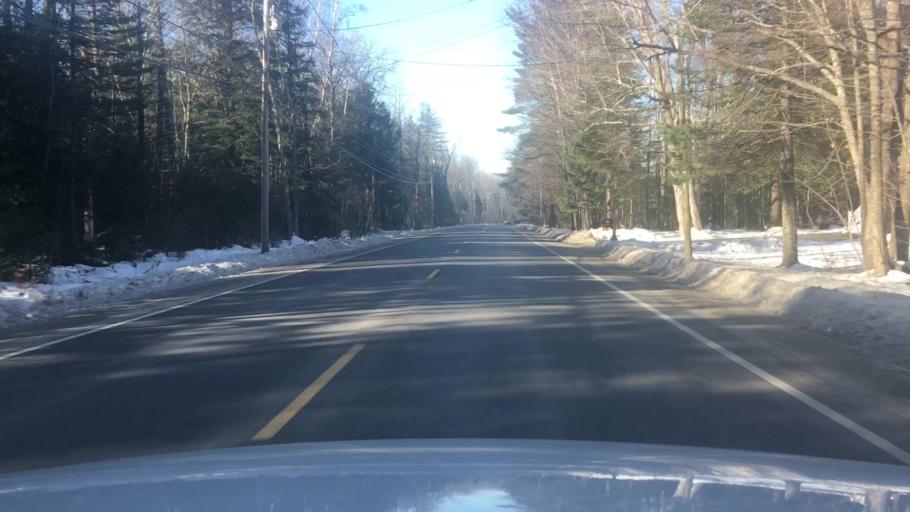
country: US
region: Maine
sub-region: Somerset County
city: Skowhegan
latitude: 44.7480
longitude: -69.7005
